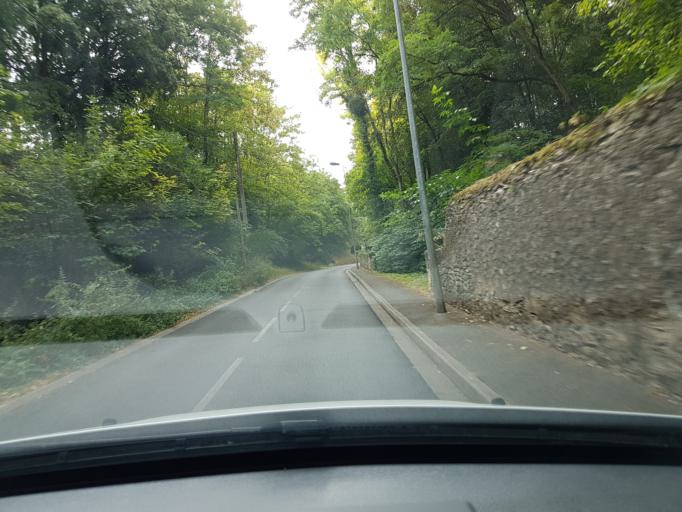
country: FR
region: Centre
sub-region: Departement d'Indre-et-Loire
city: Larcay
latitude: 47.3664
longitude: 0.7805
